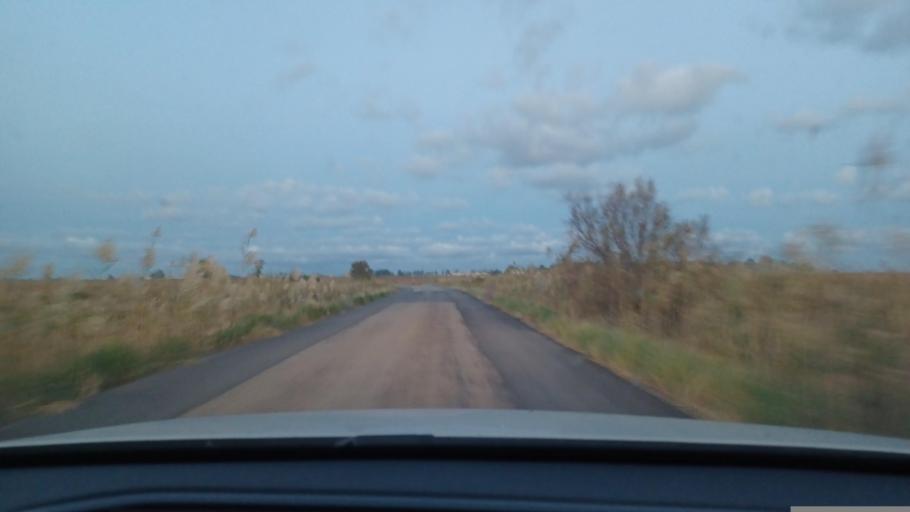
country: ES
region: Catalonia
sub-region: Provincia de Tarragona
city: Deltebre
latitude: 40.6537
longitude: 0.7686
